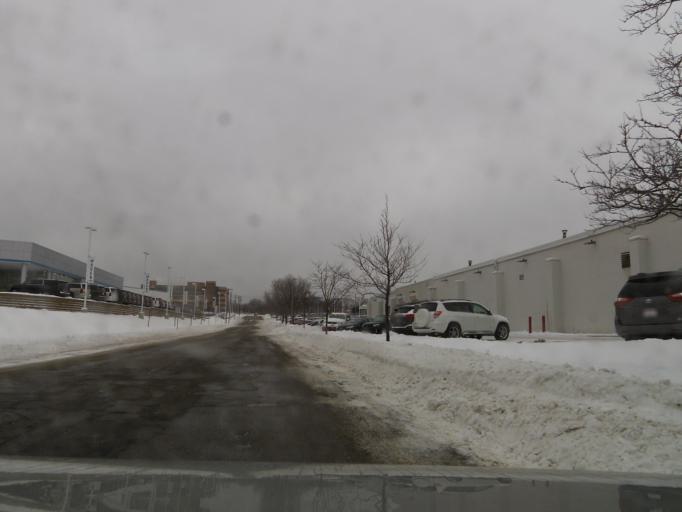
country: US
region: Minnesota
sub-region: Dakota County
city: West Saint Paul
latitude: 44.8806
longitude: -93.0854
